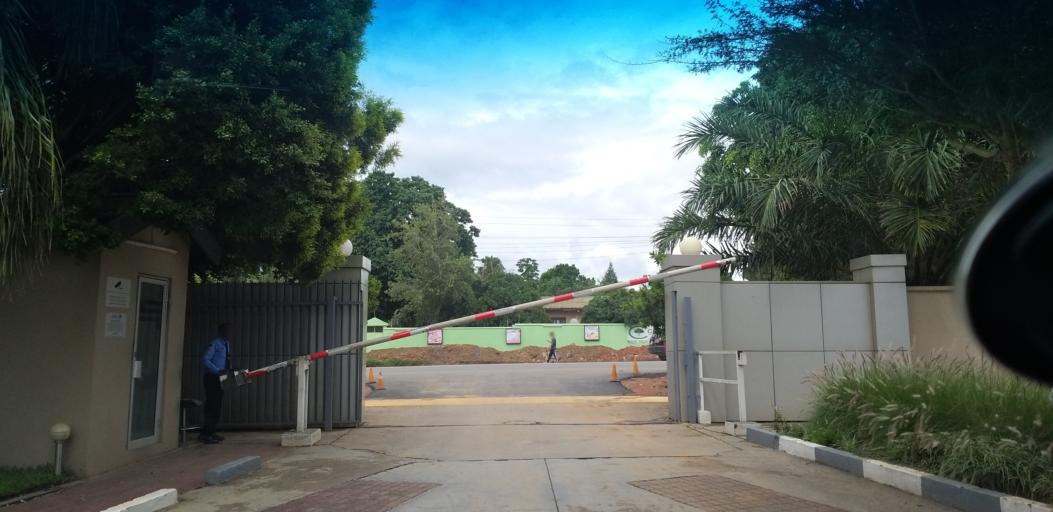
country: ZM
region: Lusaka
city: Lusaka
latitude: -15.3893
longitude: 28.3174
